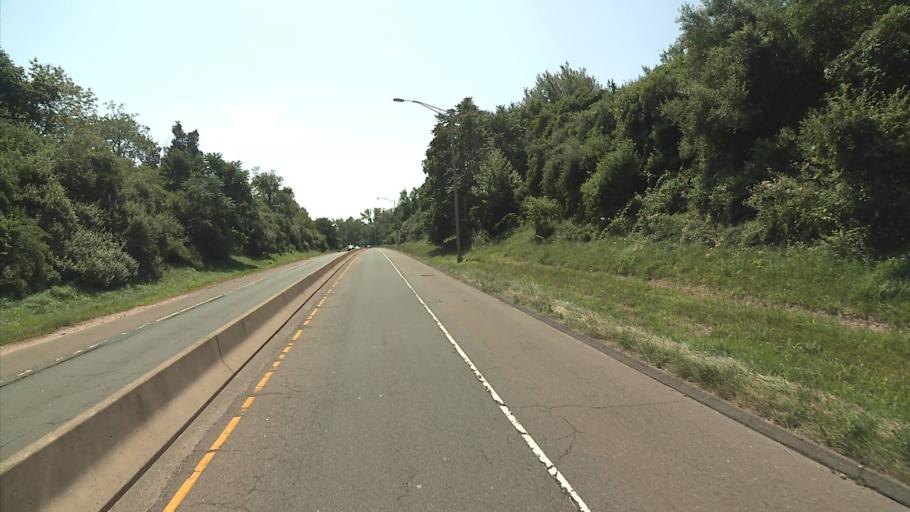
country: US
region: Connecticut
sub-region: New Haven County
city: Branford
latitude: 41.2804
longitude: -72.8345
